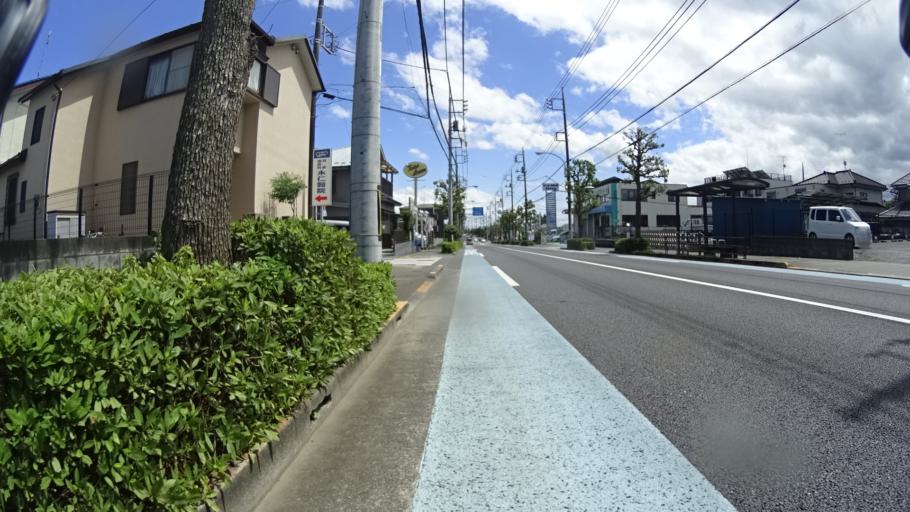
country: JP
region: Tokyo
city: Fussa
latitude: 35.7705
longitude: 139.3043
